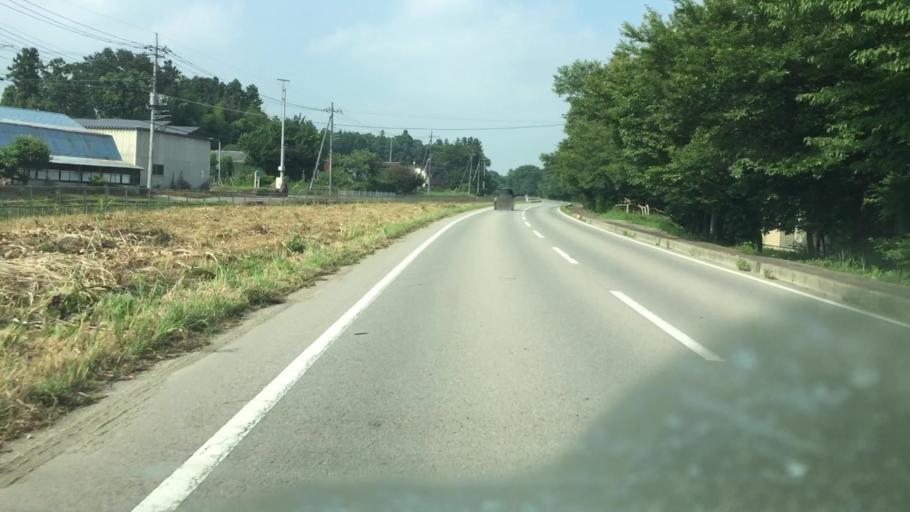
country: JP
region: Tochigi
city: Kuroiso
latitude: 37.0123
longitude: 140.0029
